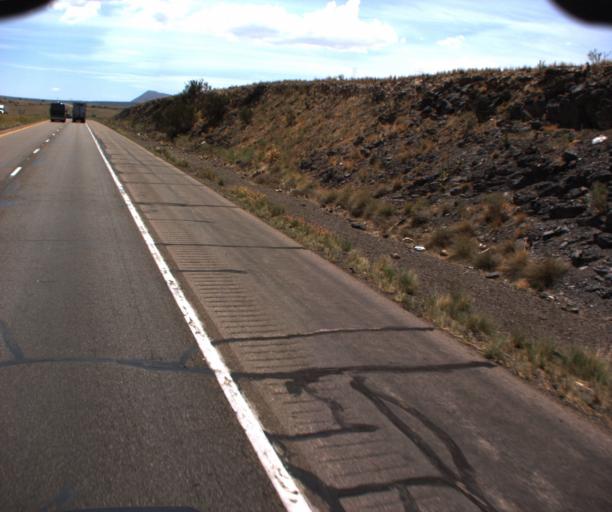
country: US
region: Arizona
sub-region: Yavapai County
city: Paulden
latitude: 35.3034
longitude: -112.8440
